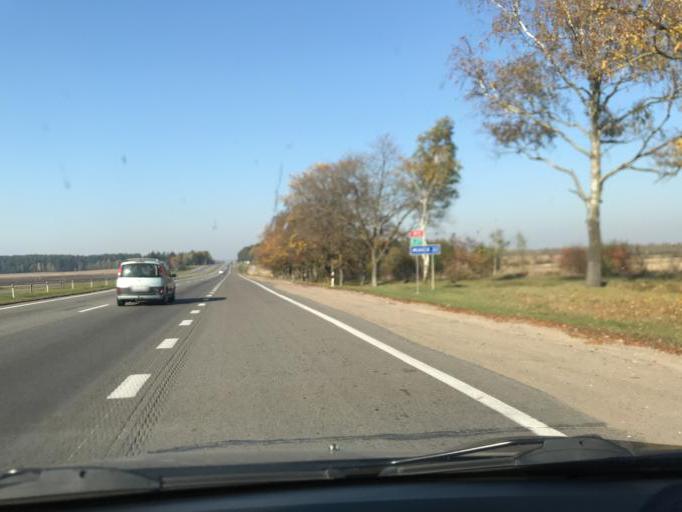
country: BY
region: Minsk
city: Dukora
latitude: 53.7066
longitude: 27.8772
